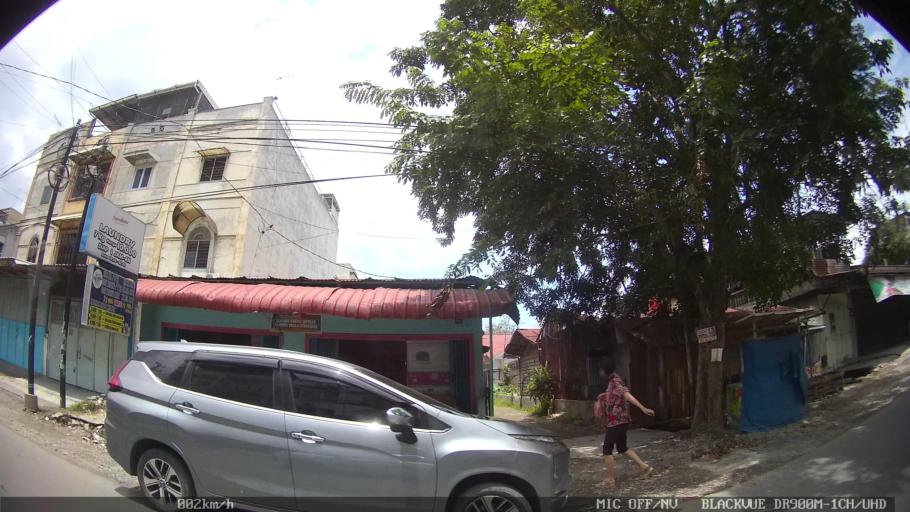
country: ID
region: North Sumatra
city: Medan
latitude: 3.6172
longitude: 98.6833
